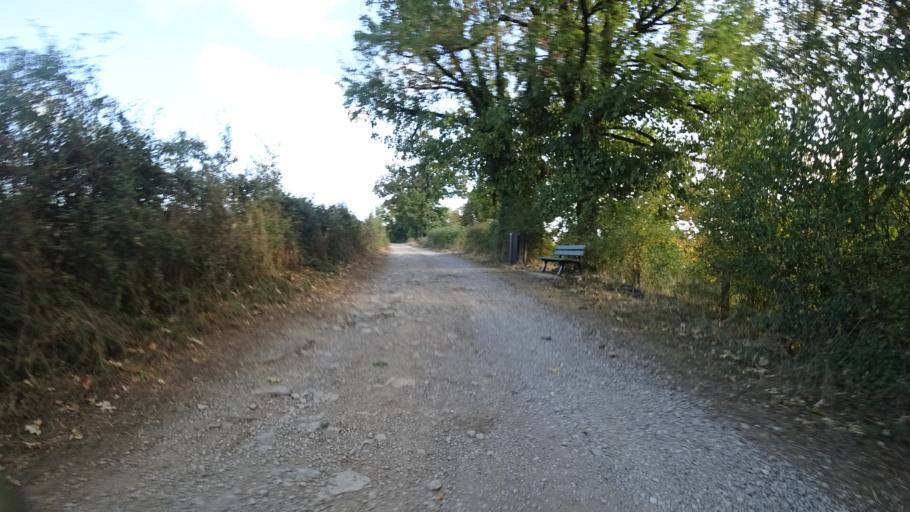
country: FR
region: Midi-Pyrenees
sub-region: Departement de l'Aveyron
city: Sebazac-Concoures
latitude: 44.3915
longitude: 2.5866
